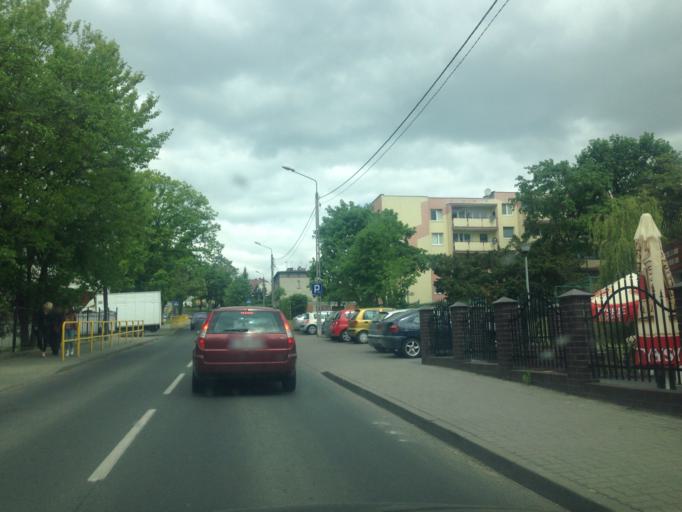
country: PL
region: Kujawsko-Pomorskie
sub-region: Powiat swiecki
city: Swiecie
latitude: 53.4111
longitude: 18.4456
